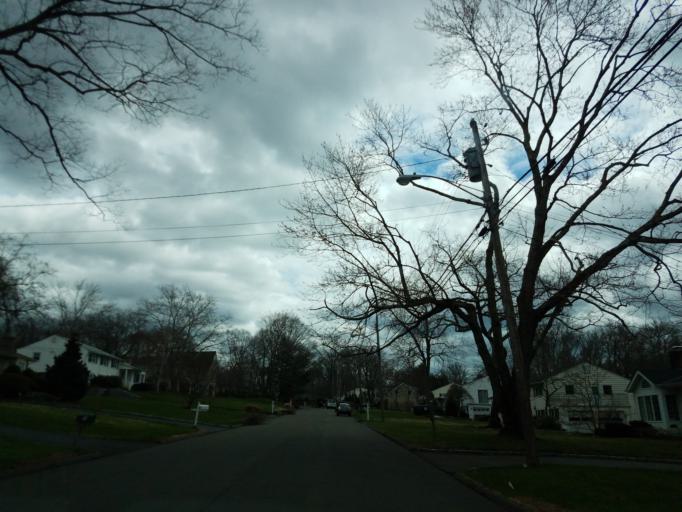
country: US
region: Connecticut
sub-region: Fairfield County
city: Stamford
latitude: 41.0956
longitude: -73.5368
